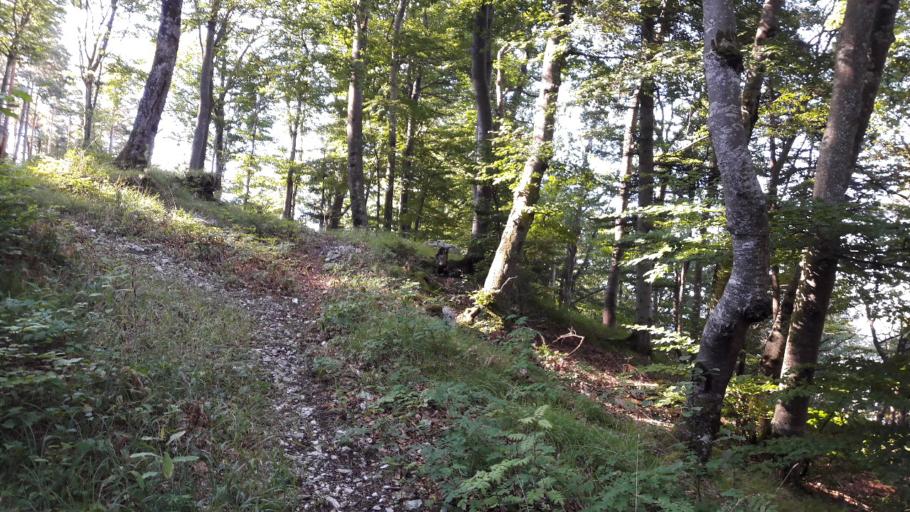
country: CH
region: Solothurn
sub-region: Bezirk Thal
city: Laupersdorf
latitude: 47.3277
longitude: 7.6521
